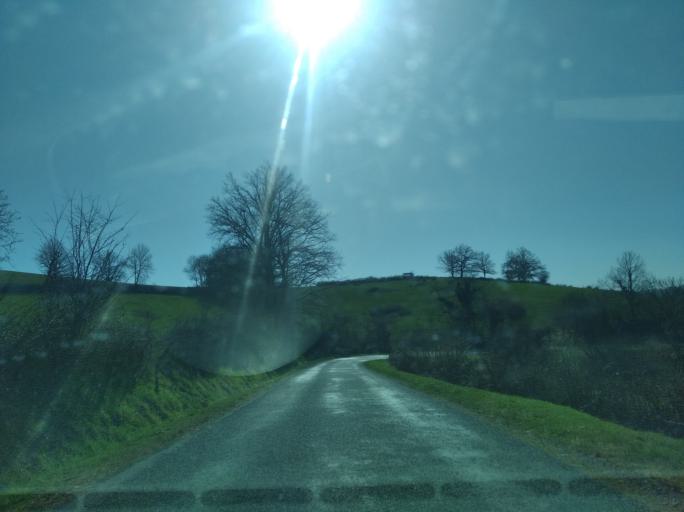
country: FR
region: Auvergne
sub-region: Departement de l'Allier
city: Le Mayet-de-Montagne
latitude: 46.0972
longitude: 3.6787
